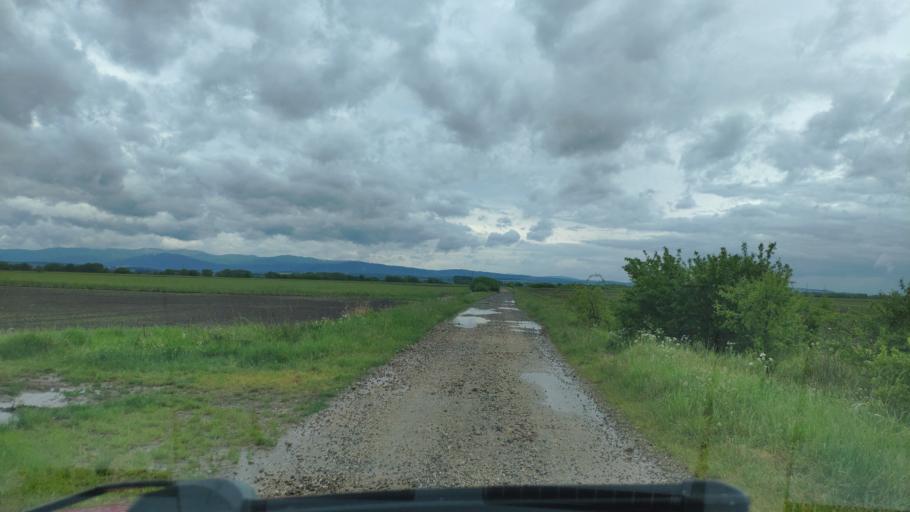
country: SK
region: Kosicky
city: Moldava nad Bodvou
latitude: 48.5477
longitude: 21.1132
